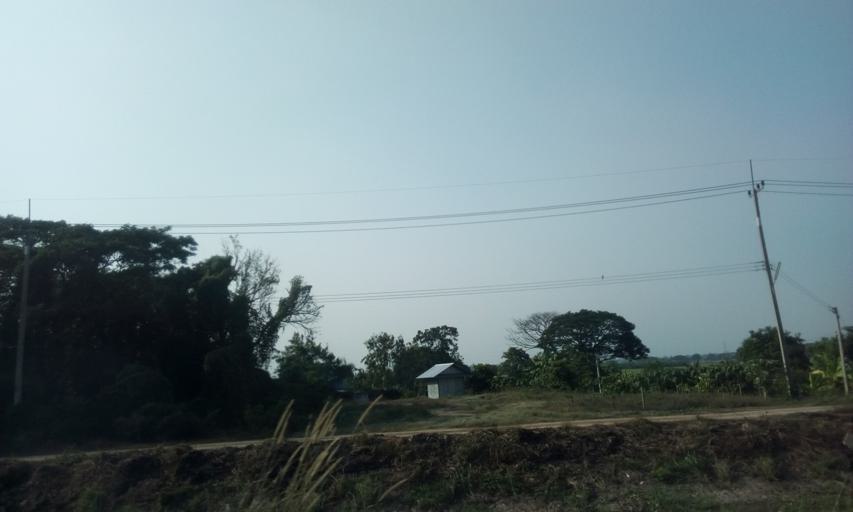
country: TH
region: Sing Buri
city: Tha Chang
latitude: 14.7342
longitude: 100.4336
